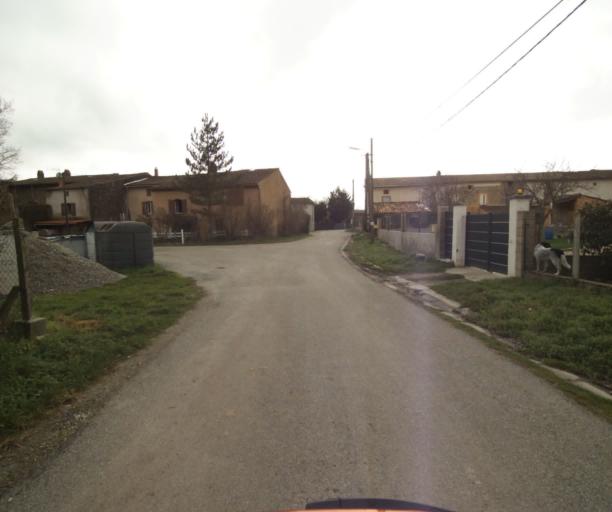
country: FR
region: Languedoc-Roussillon
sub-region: Departement de l'Aude
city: Belpech
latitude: 43.1713
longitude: 1.6882
